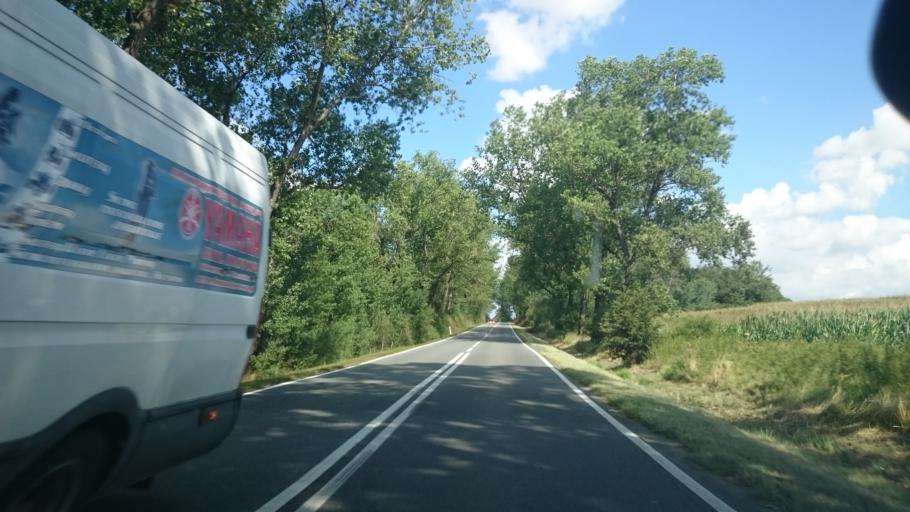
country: PL
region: Lower Silesian Voivodeship
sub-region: Powiat zabkowicki
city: Kamieniec Zabkowicki
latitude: 50.5473
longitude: 16.8604
